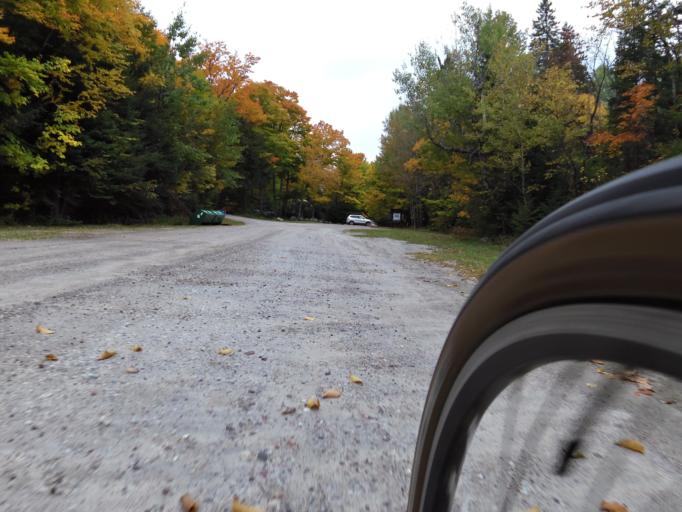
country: CA
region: Quebec
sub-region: Outaouais
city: Wakefield
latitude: 45.6018
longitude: -76.0420
